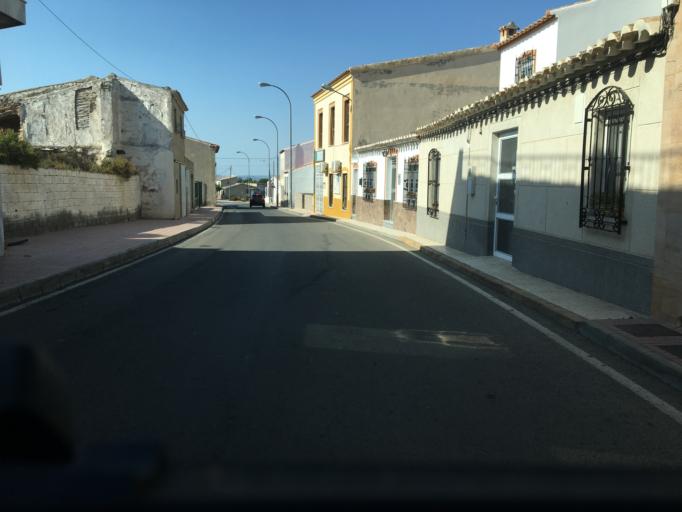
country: ES
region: Andalusia
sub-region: Provincia de Almeria
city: Huercal-Overa
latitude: 37.4615
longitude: -1.9893
